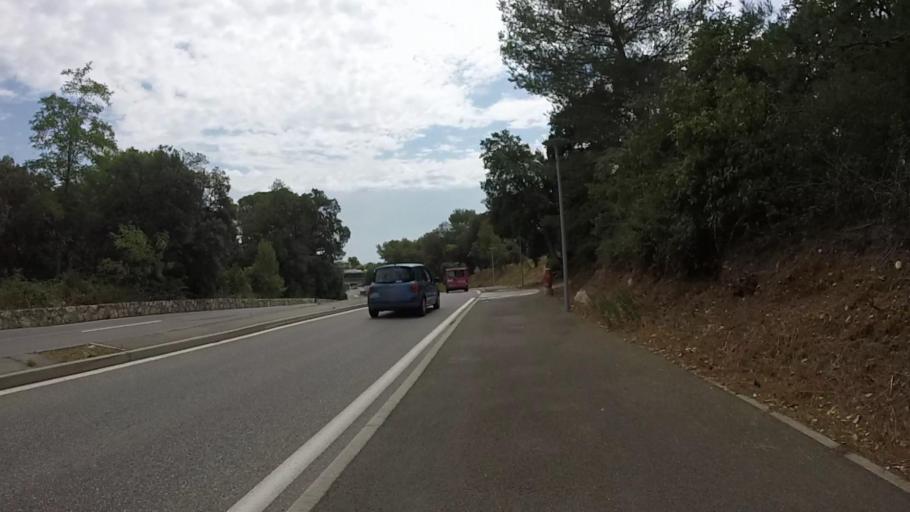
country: FR
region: Provence-Alpes-Cote d'Azur
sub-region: Departement des Alpes-Maritimes
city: Biot
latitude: 43.6147
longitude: 7.0866
